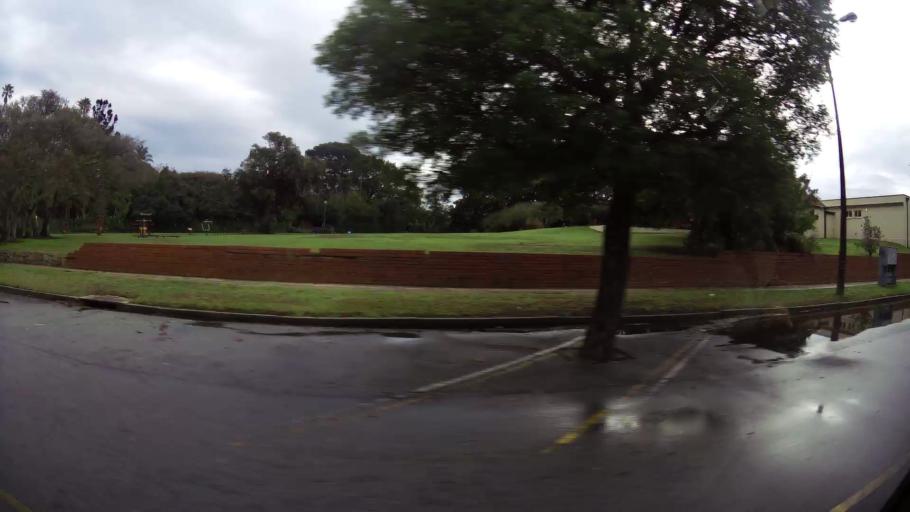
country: ZA
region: Eastern Cape
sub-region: Nelson Mandela Bay Metropolitan Municipality
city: Port Elizabeth
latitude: -33.9678
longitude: 25.6064
